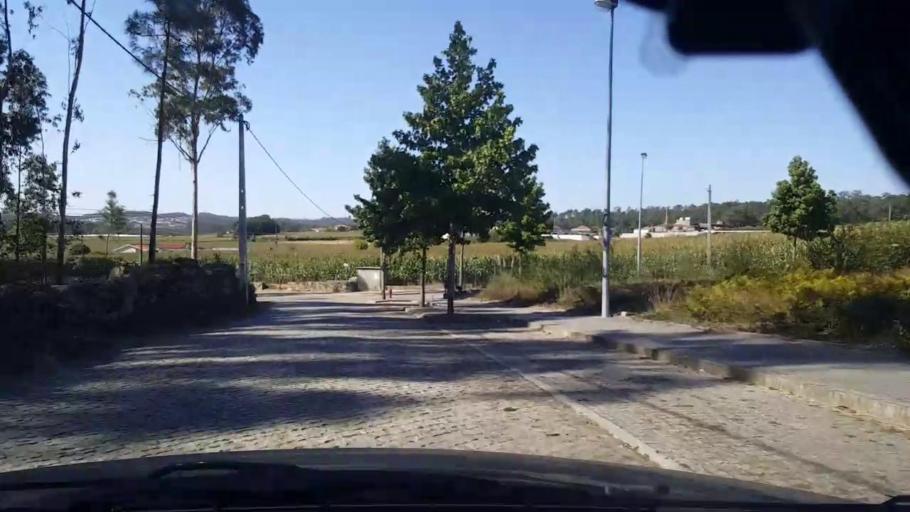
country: PT
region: Braga
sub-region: Vila Nova de Famalicao
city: Ribeirao
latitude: 41.3569
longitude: -8.6328
